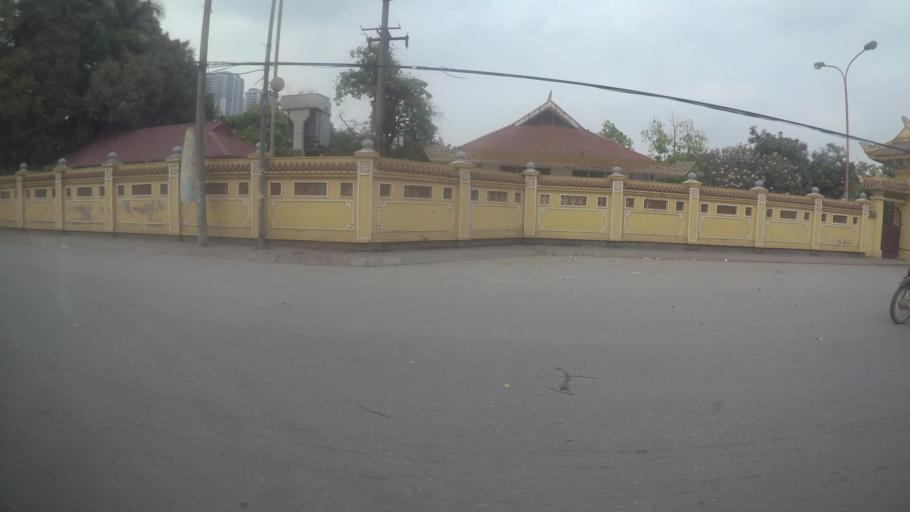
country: VN
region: Ha Noi
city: Cau Dien
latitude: 21.0392
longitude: 105.7692
